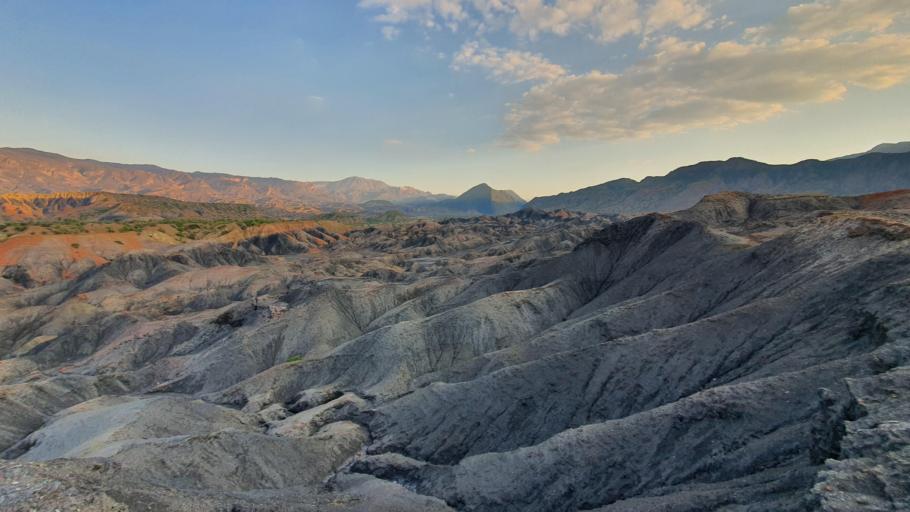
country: BO
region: Chuquisaca
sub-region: Provincia Zudanez
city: Mojocoya
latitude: -18.6887
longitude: -64.5145
